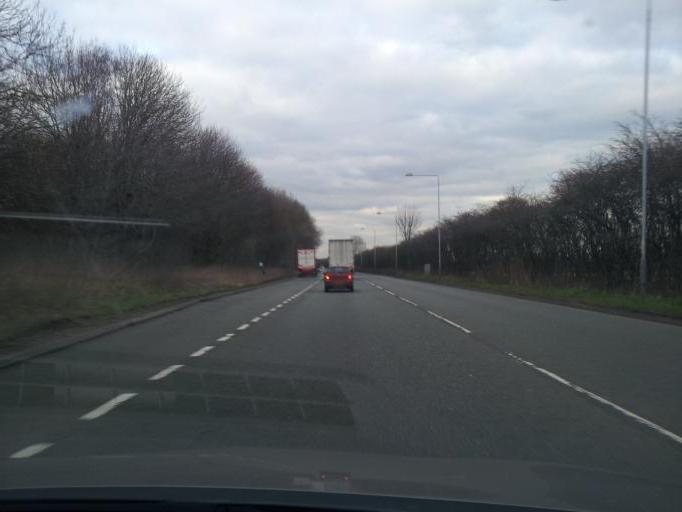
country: GB
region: England
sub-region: Nottinghamshire
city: West Bridgford
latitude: 52.9149
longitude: -1.1011
